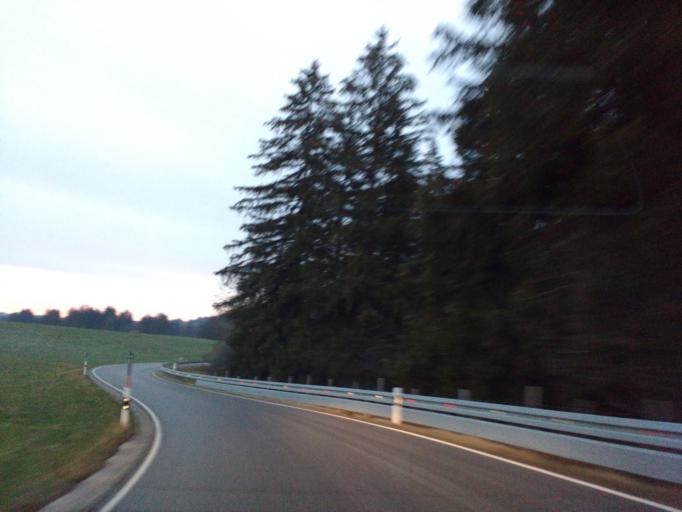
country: DE
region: Bavaria
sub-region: Upper Bavaria
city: Bernbeuren
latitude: 47.7527
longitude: 10.7682
